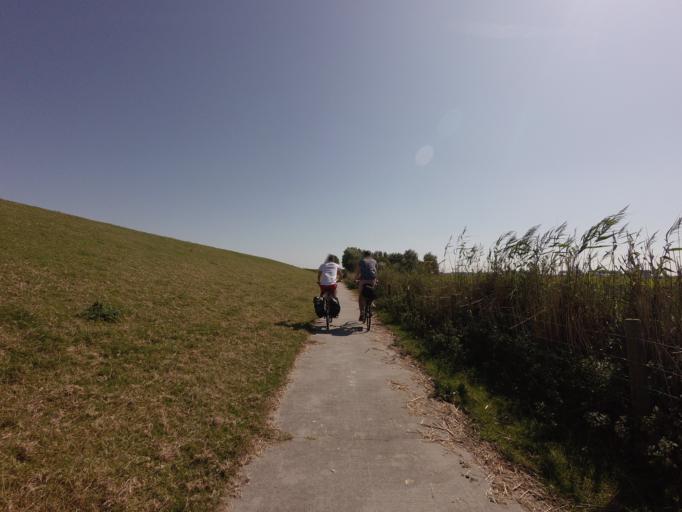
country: NL
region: Friesland
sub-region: Gemeente Dongeradeel
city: Anjum
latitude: 53.3982
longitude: 6.1030
